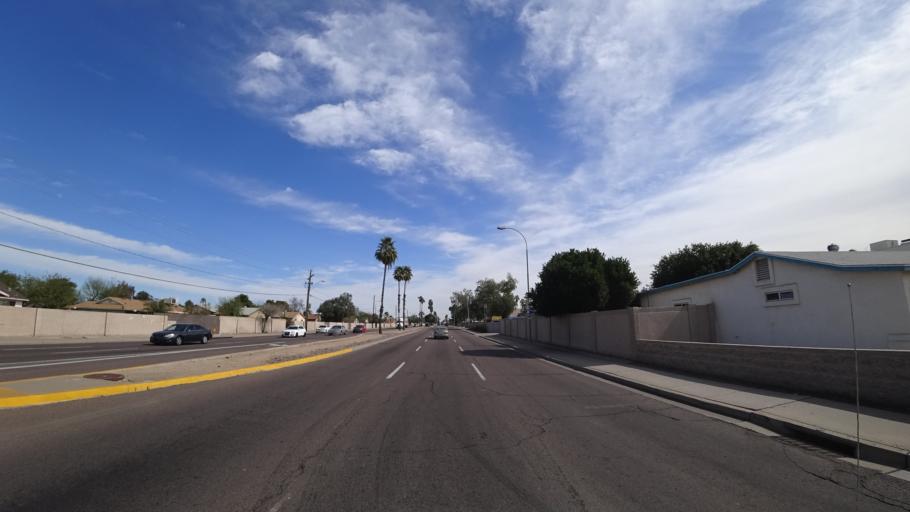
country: US
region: Arizona
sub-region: Maricopa County
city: Tolleson
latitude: 33.4802
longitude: -112.2159
